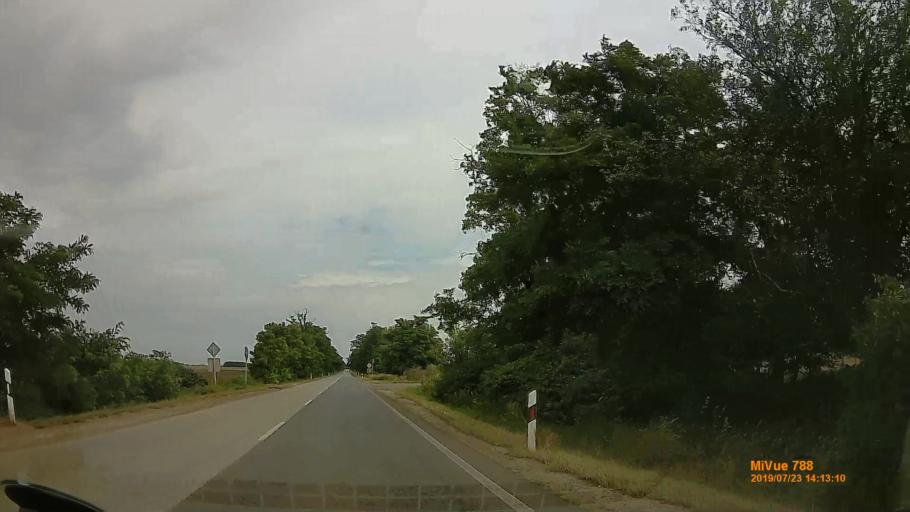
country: HU
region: Szabolcs-Szatmar-Bereg
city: Nagycserkesz
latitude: 47.9584
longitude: 21.4675
